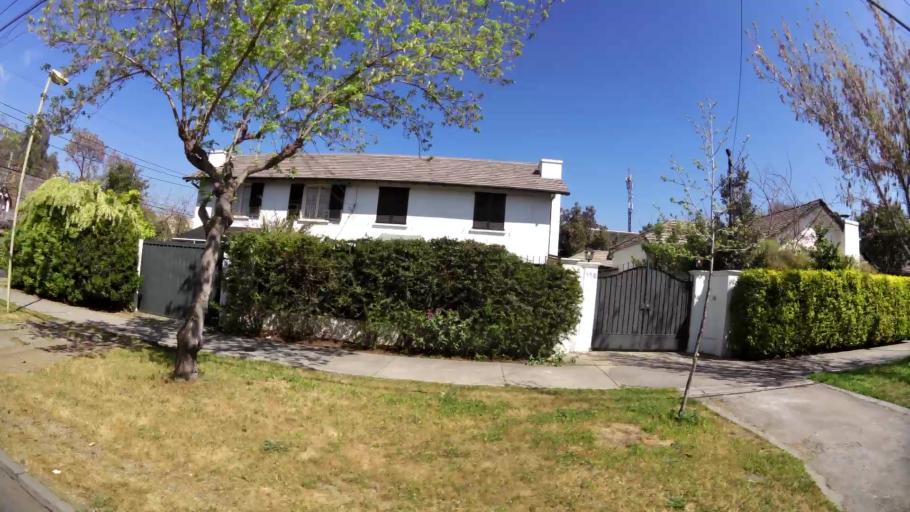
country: CL
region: Santiago Metropolitan
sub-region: Provincia de Santiago
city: Villa Presidente Frei, Nunoa, Santiago, Chile
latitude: -33.4150
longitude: -70.5744
